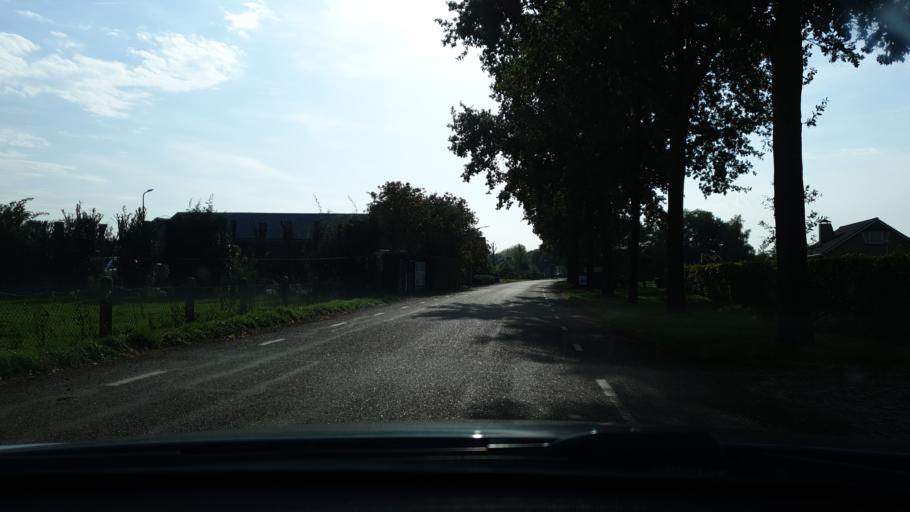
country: NL
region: Gelderland
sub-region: Gemeente Wijchen
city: Bergharen
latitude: 51.8751
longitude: 5.7008
